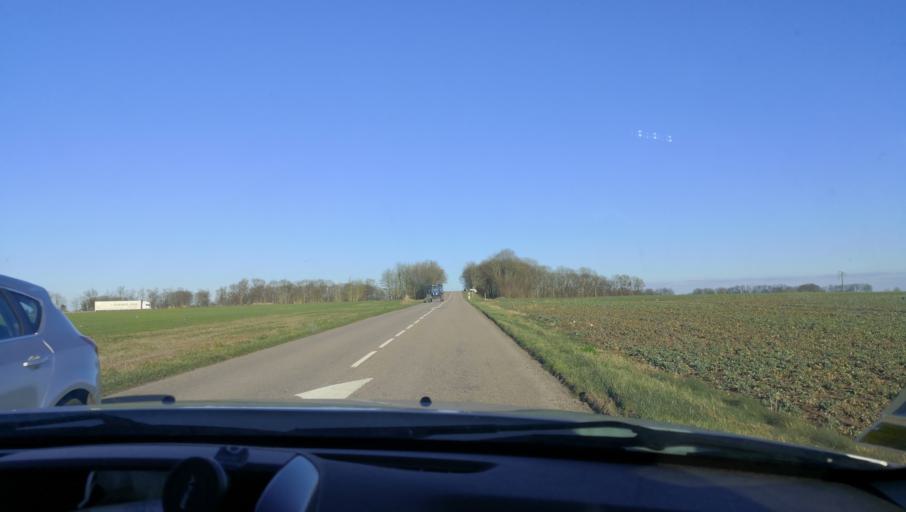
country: FR
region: Haute-Normandie
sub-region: Departement de la Seine-Maritime
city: Totes
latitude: 49.6706
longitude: 1.0350
